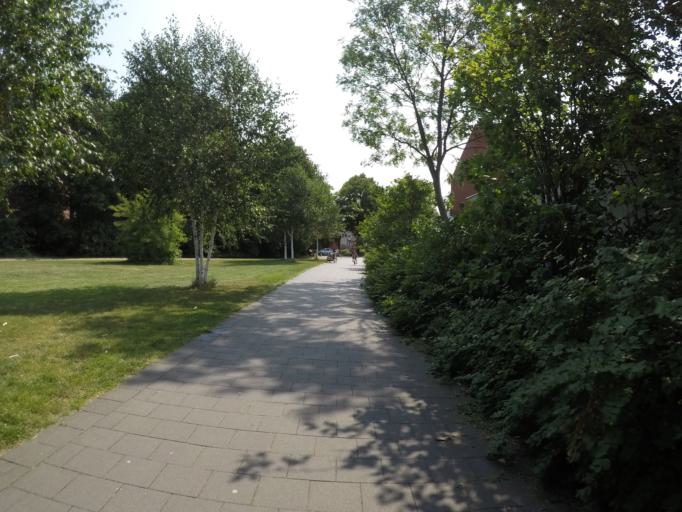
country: DE
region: Hamburg
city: Kleiner Grasbrook
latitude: 53.5068
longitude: 9.9852
